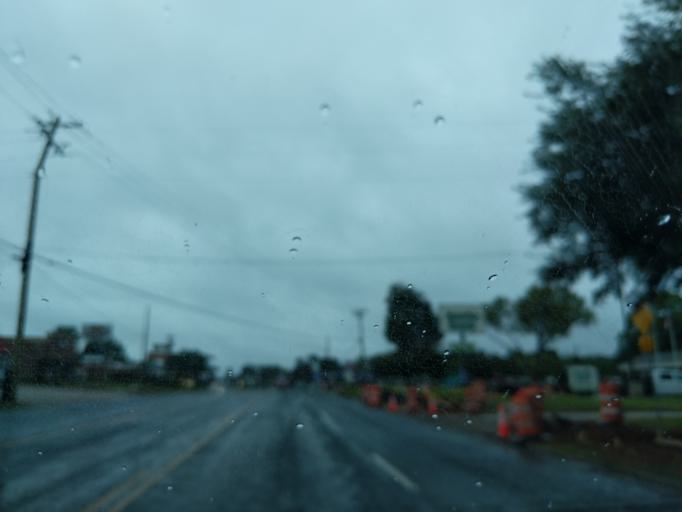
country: US
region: Texas
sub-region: Nacogdoches County
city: Nacogdoches
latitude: 31.6322
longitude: -94.6527
